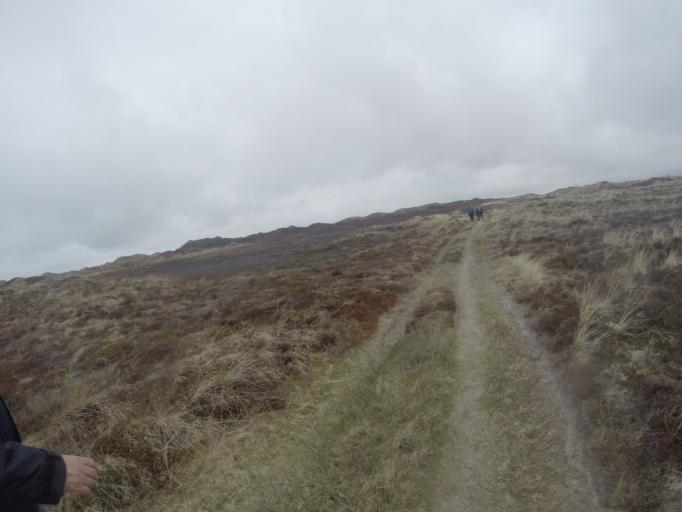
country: DK
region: Central Jutland
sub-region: Lemvig Kommune
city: Thyboron
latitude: 56.8443
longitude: 8.2779
